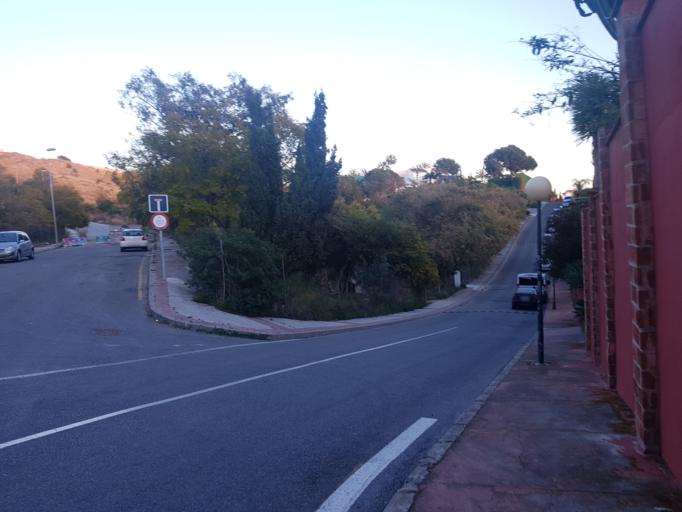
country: ES
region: Andalusia
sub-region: Provincia de Malaga
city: Marbella
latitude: 36.5227
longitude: -4.8887
